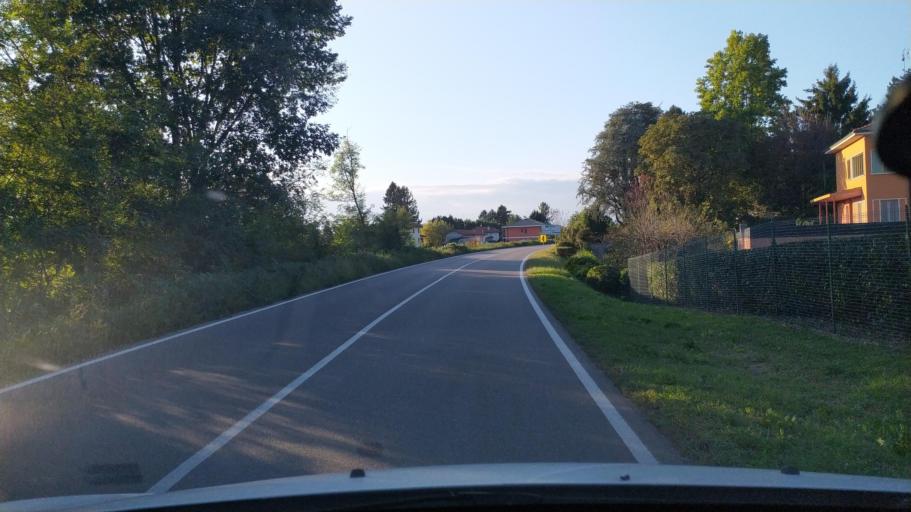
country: IT
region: Lombardy
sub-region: Provincia di Varese
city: Golasecca
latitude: 45.7004
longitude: 8.6635
